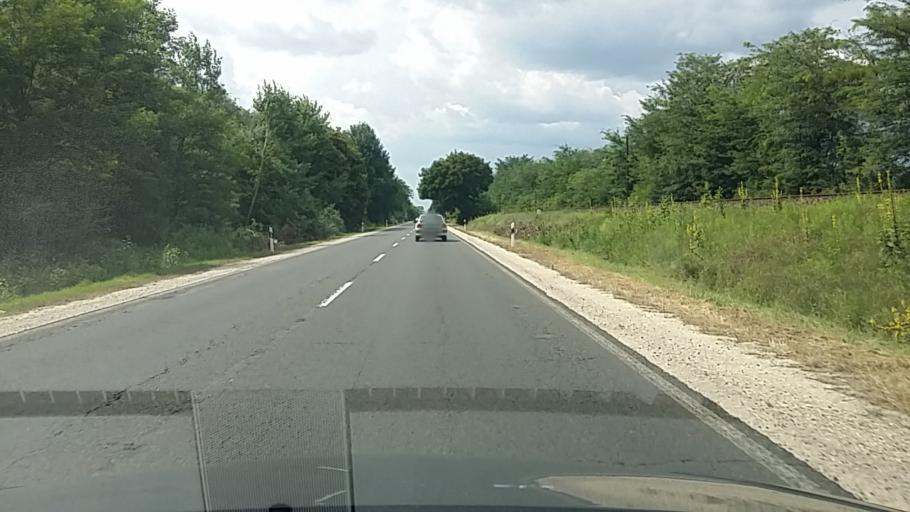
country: HU
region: Pest
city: Ujhartyan
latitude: 47.1724
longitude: 19.3655
